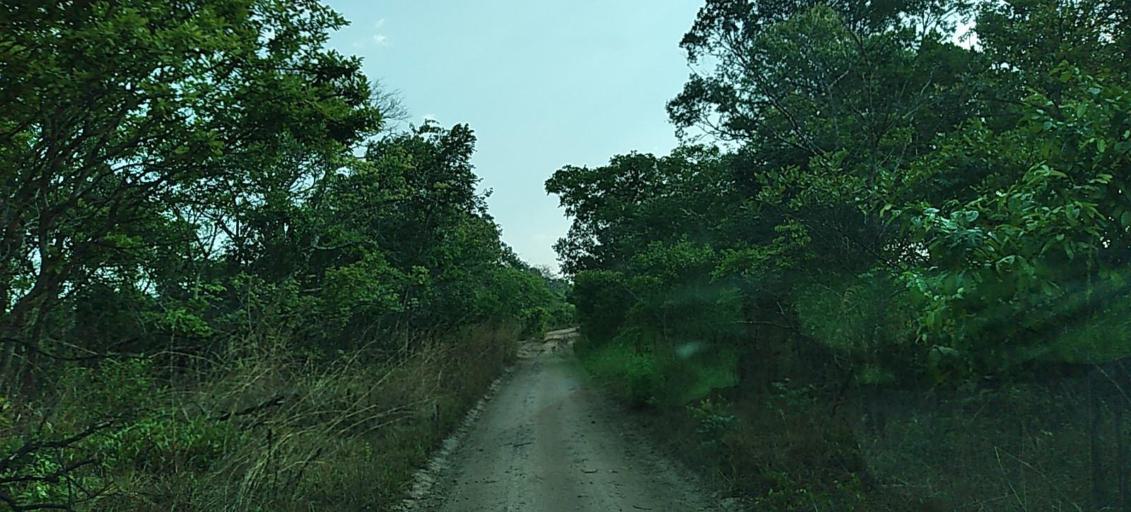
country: ZM
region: North-Western
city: Mwinilunga
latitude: -11.3270
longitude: 24.7379
